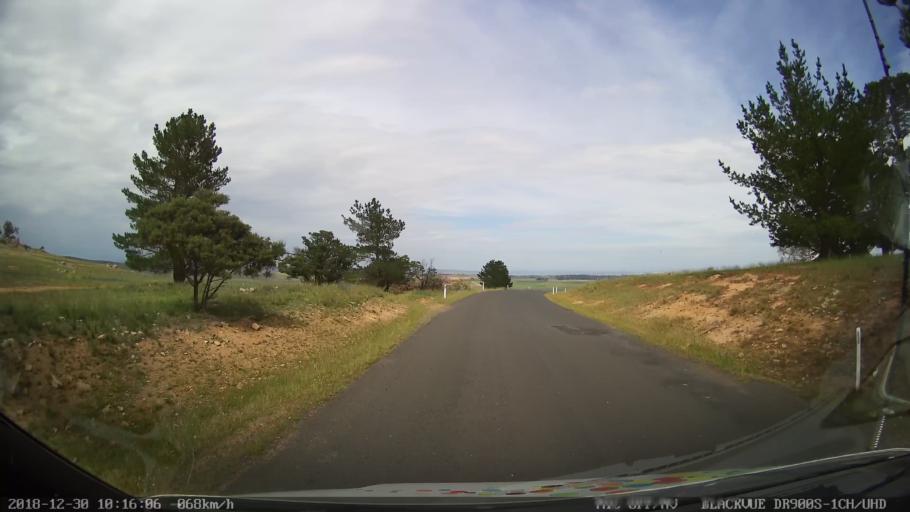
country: AU
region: New South Wales
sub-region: Snowy River
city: Berridale
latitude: -36.5475
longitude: 149.0391
